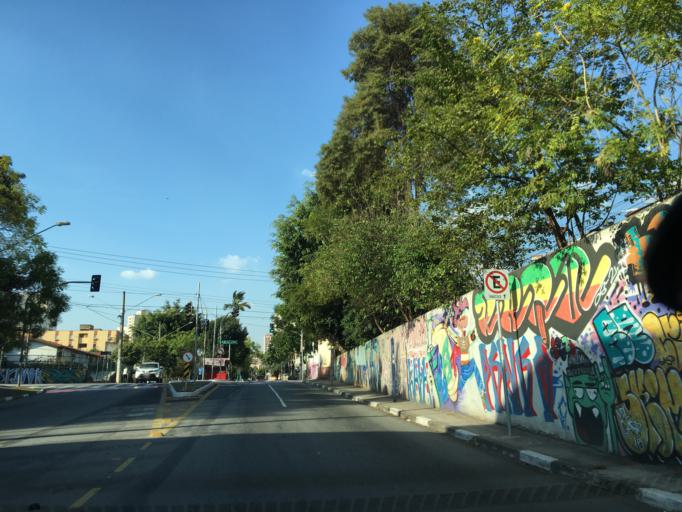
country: BR
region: Sao Paulo
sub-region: Sao Paulo
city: Sao Paulo
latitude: -23.4756
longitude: -46.6391
